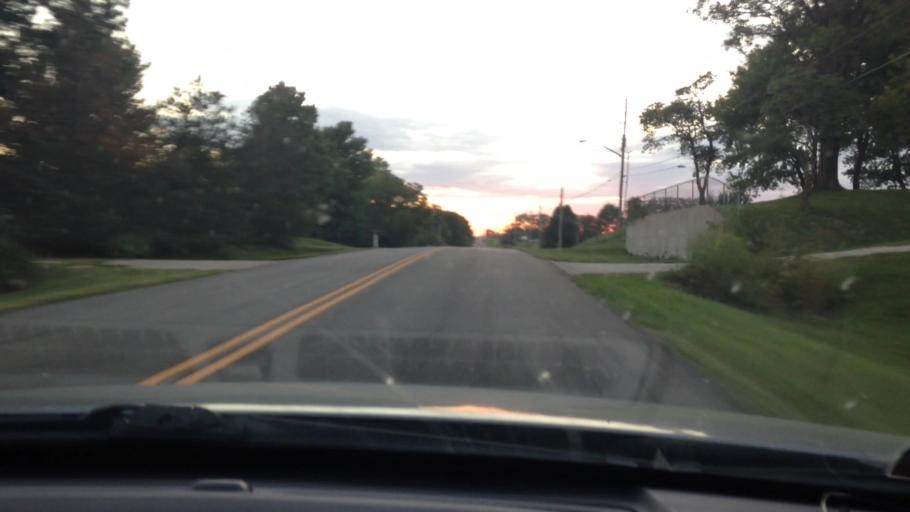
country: US
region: Kansas
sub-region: Leavenworth County
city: Lansing
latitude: 39.1868
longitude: -94.8908
